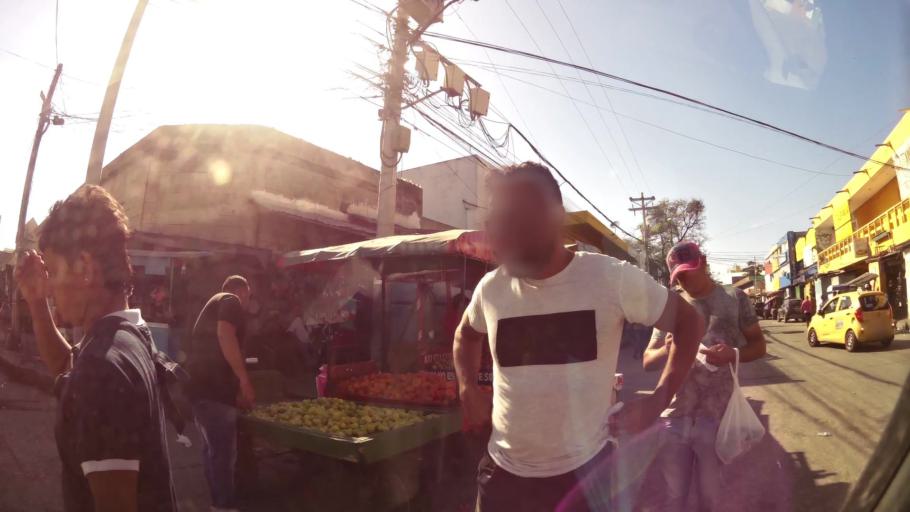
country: CO
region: Atlantico
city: Barranquilla
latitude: 10.9783
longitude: -74.7775
